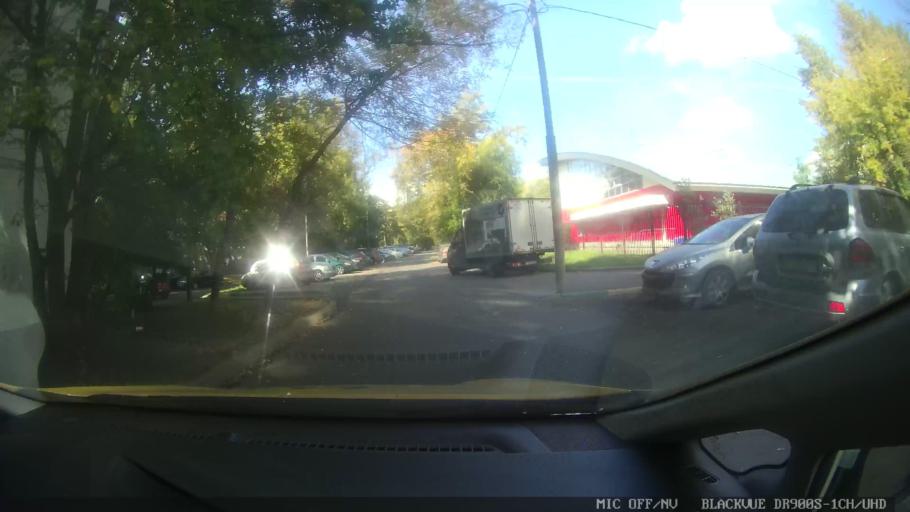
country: RU
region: Moscow
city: Novokuz'minki
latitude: 55.7003
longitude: 37.7821
